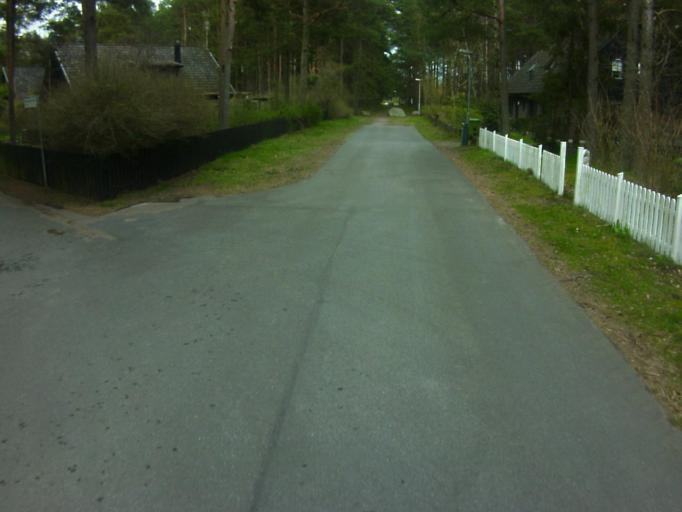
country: SE
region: Skane
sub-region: Kavlinge Kommun
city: Hofterup
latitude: 55.7968
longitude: 12.9748
